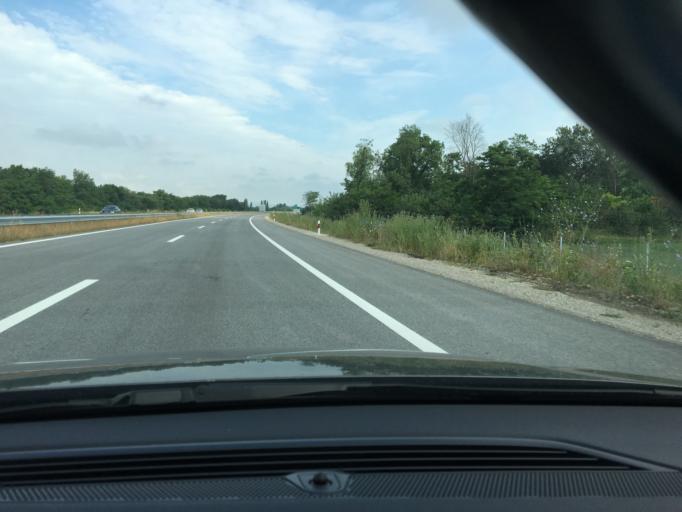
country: MK
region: Sveti Nikole
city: Sveti Nikole
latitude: 41.8494
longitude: 21.9680
